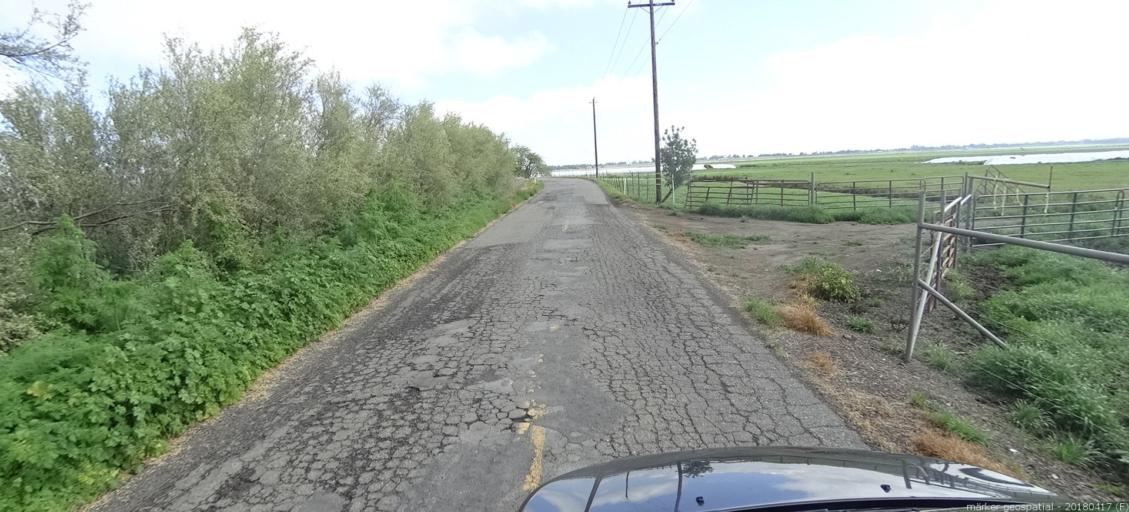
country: US
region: California
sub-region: Sacramento County
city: Walnut Grove
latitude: 38.2488
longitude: -121.5596
